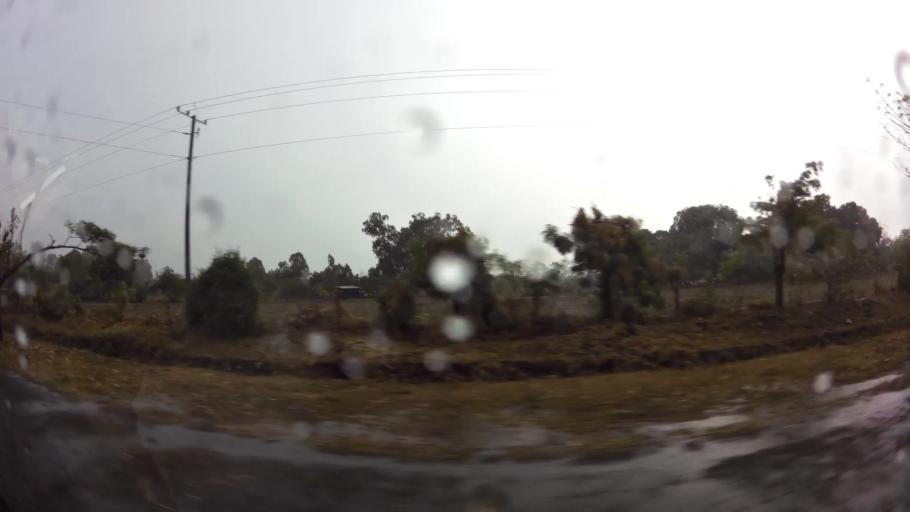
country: NI
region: Leon
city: Telica
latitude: 12.5291
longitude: -86.8562
